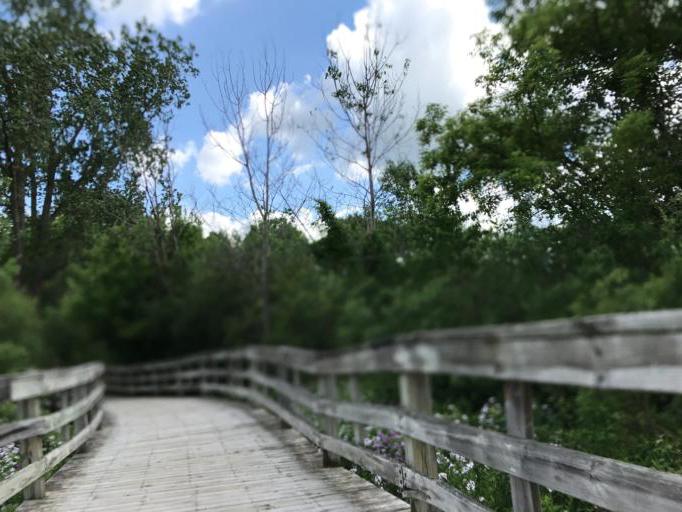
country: US
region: Michigan
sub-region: Oakland County
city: South Lyon
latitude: 42.4555
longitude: -83.6619
